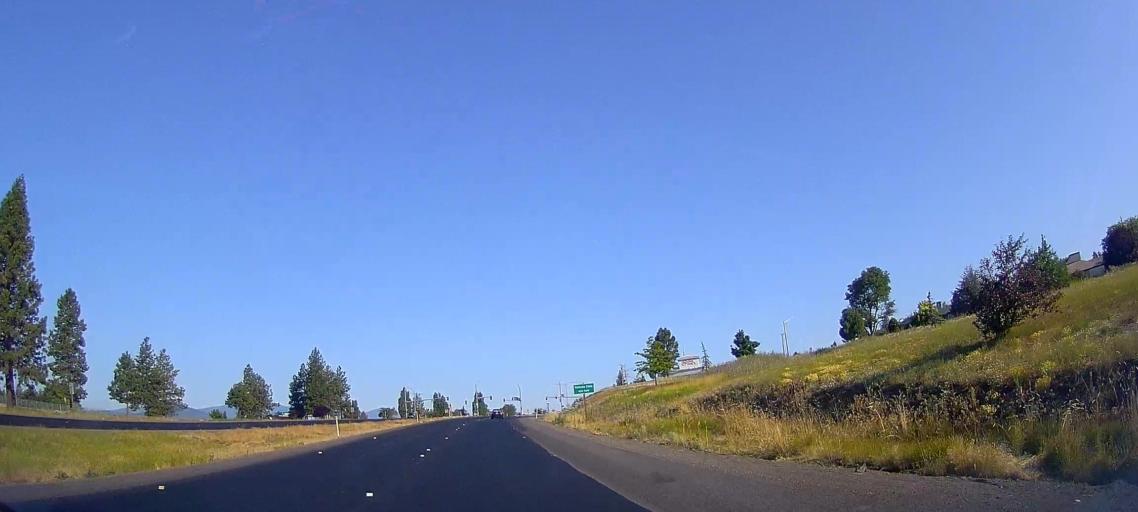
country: US
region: Oregon
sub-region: Klamath County
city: Klamath Falls
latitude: 42.2472
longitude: -121.7891
